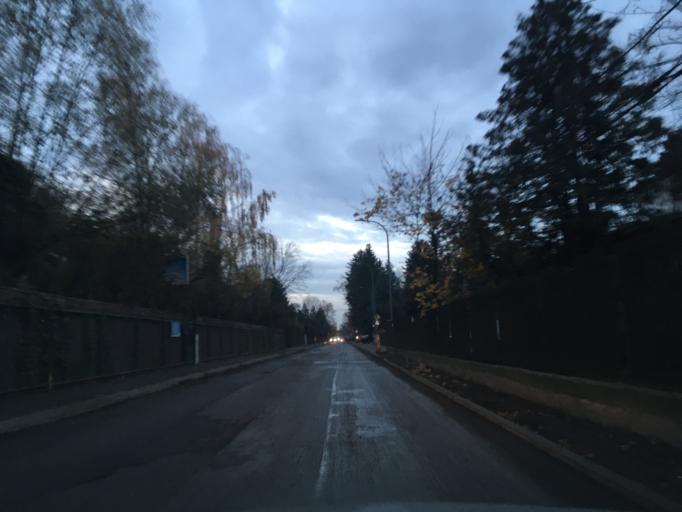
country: PL
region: Masovian Voivodeship
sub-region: Powiat piaseczynski
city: Piaseczno
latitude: 52.0545
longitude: 20.9848
